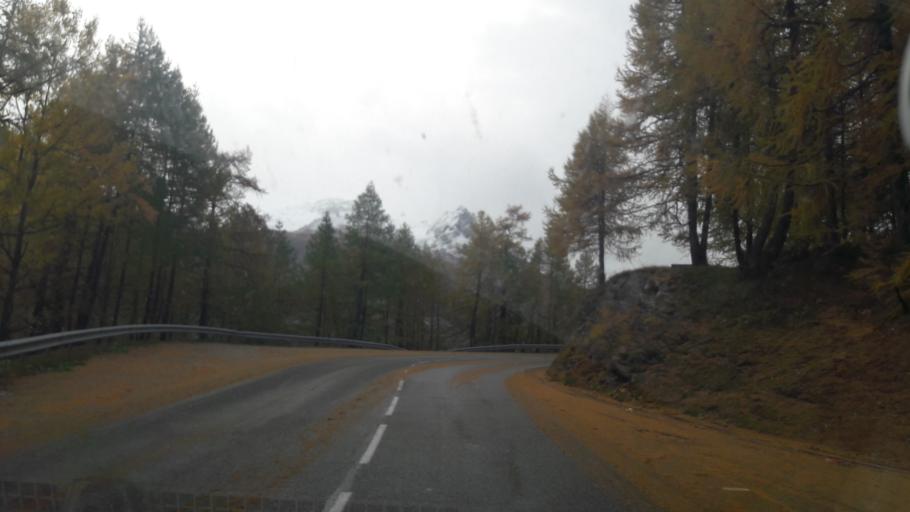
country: FR
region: Rhone-Alpes
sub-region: Departement de la Savoie
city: Tignes
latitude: 45.4868
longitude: 6.9280
